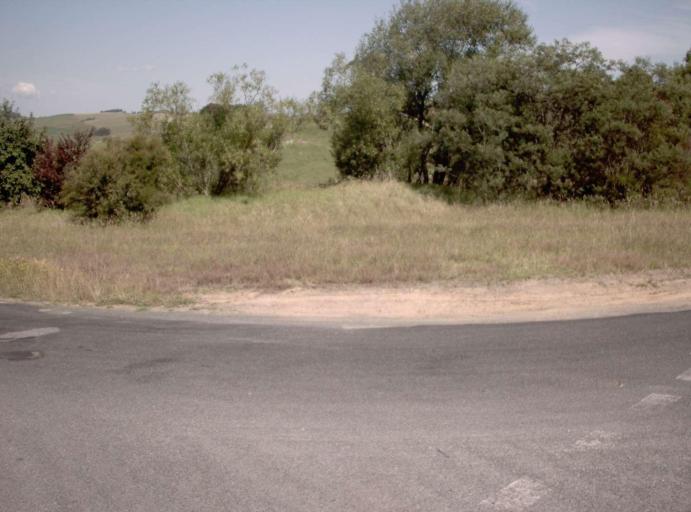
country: AU
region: Victoria
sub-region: Cardinia
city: Bunyip
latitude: -38.3132
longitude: 145.7709
